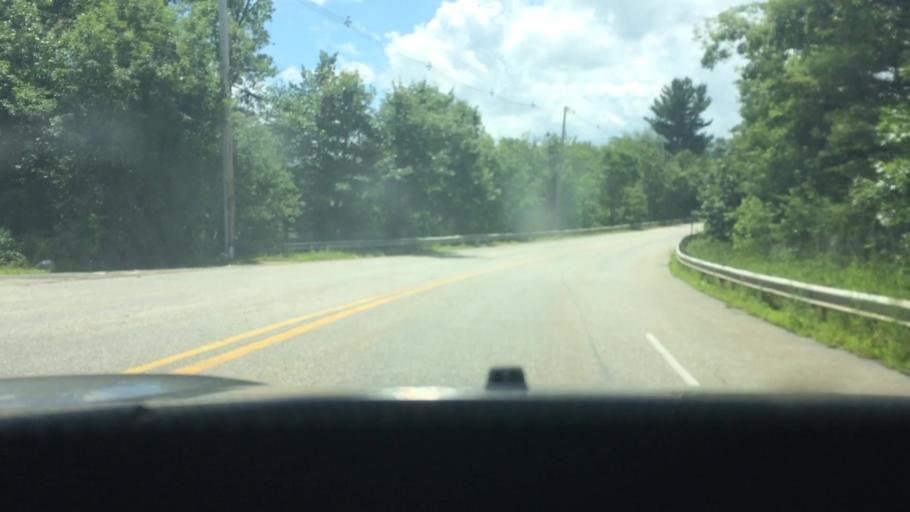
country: US
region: Massachusetts
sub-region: Middlesex County
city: Shirley
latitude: 42.5230
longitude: -71.6323
